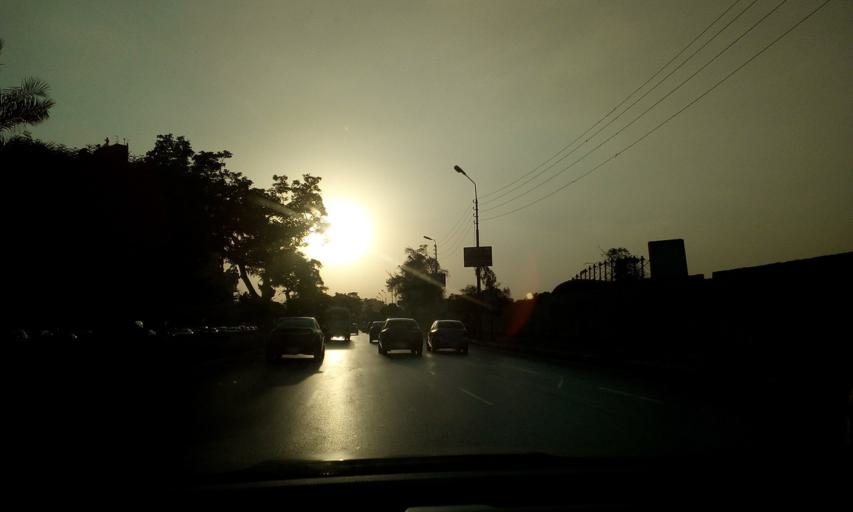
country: EG
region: Muhafazat al Qalyubiyah
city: Al Khankah
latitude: 30.1191
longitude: 31.3548
